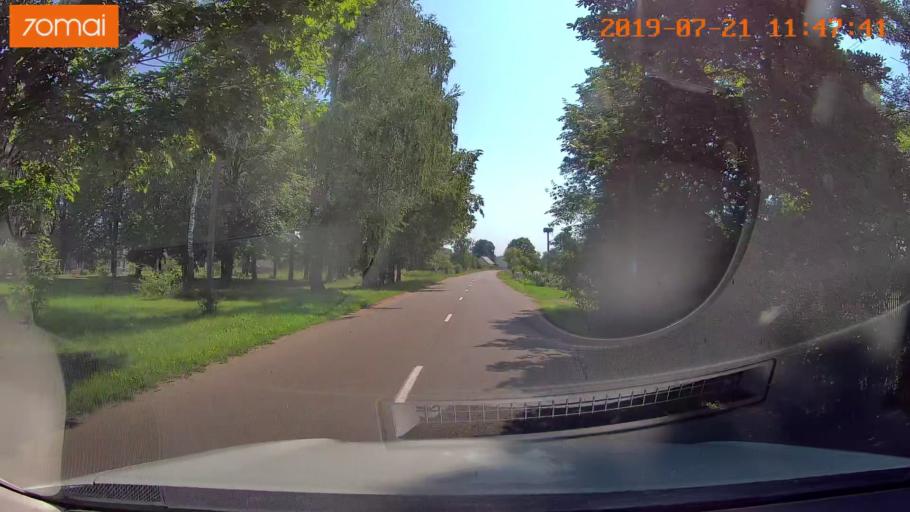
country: BY
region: Grodnenskaya
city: Lyubcha
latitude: 53.9017
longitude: 26.0513
